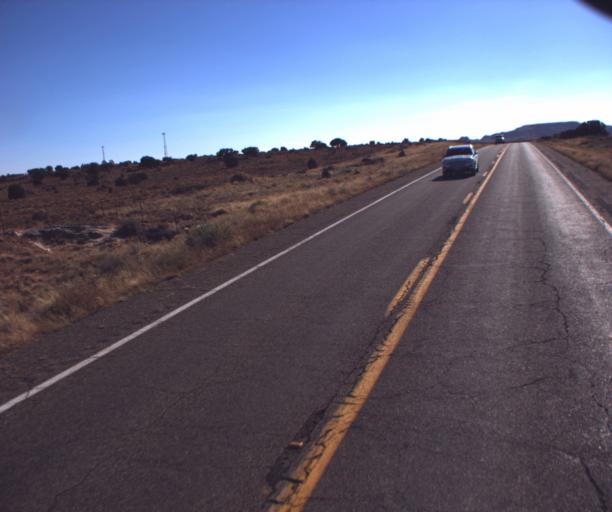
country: US
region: Arizona
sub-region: Coconino County
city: Kaibito
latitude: 36.5909
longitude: -111.0997
